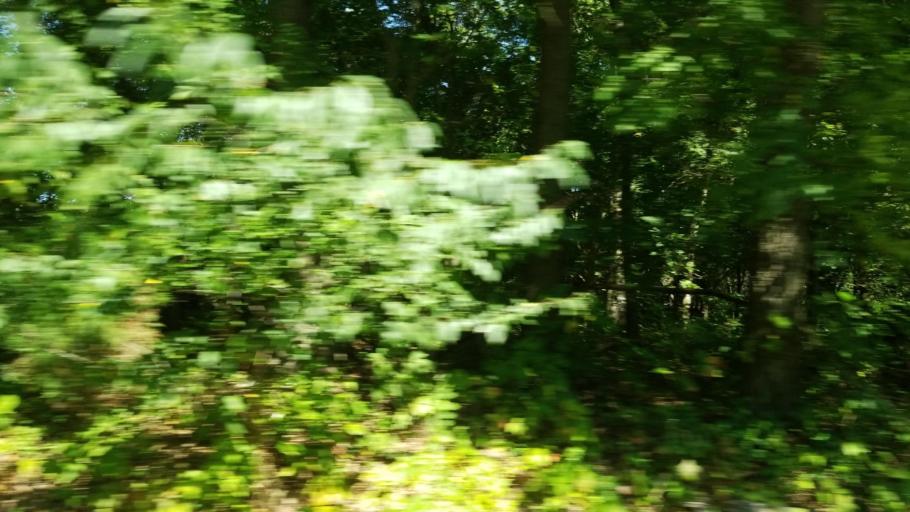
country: US
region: Illinois
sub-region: Saline County
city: Carrier Mills
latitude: 37.7954
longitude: -88.6471
